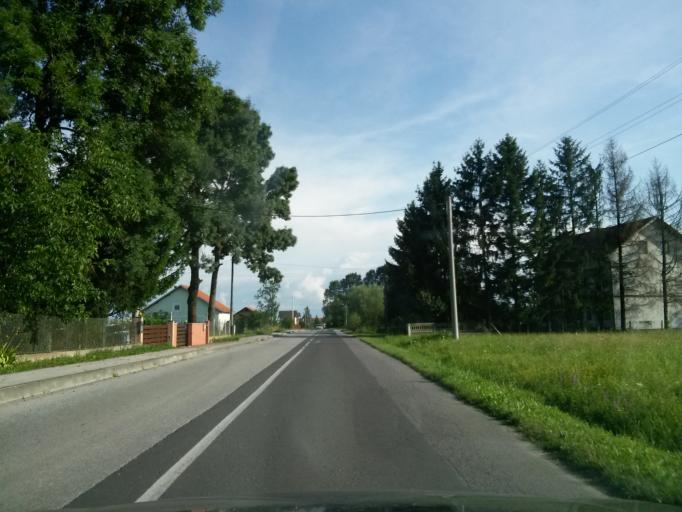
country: HR
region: Grad Zagreb
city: Horvati
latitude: 45.6013
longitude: 15.8483
